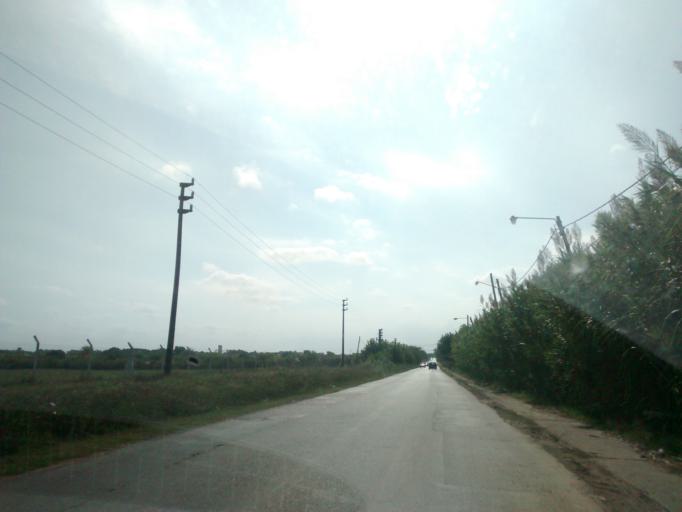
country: AR
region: Buenos Aires
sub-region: Partido de La Plata
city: La Plata
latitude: -34.9676
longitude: -57.8797
